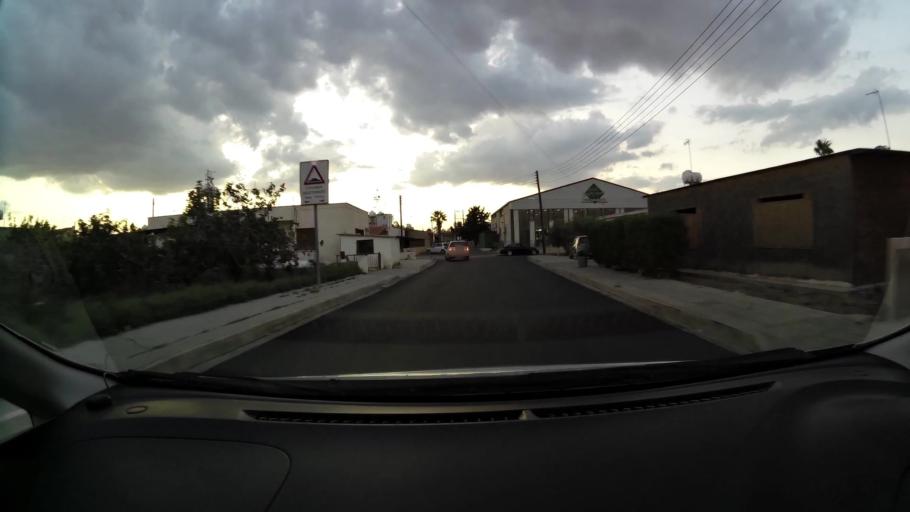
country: CY
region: Larnaka
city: Dhromolaxia
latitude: 34.8736
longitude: 33.5837
